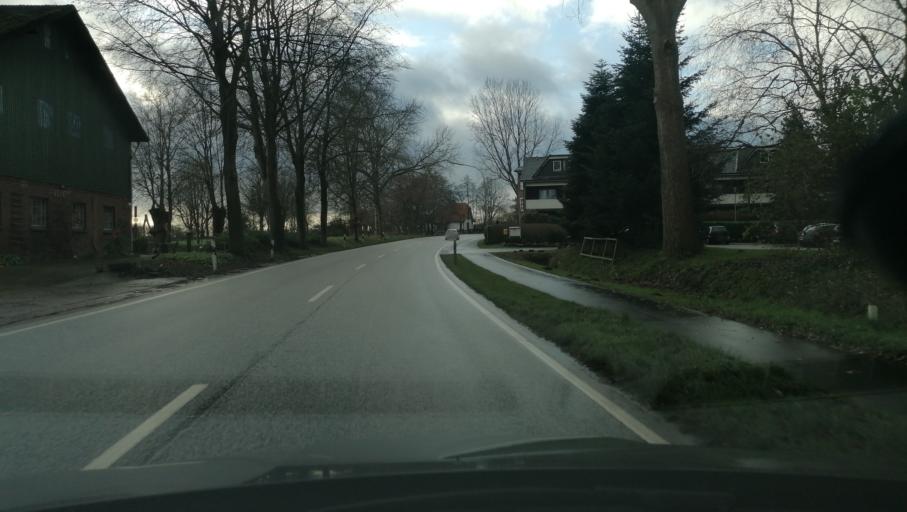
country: DE
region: Schleswig-Holstein
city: Sarzbuttel
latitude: 54.1001
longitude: 9.1842
